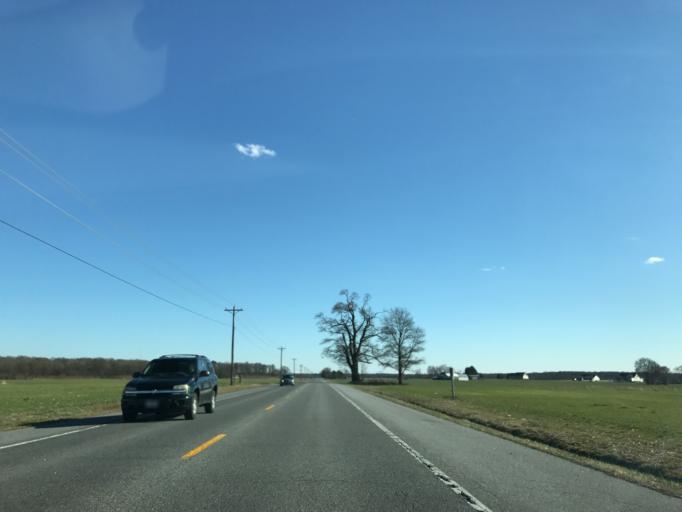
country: US
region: Maryland
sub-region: Caroline County
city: Greensboro
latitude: 39.0801
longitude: -75.8618
